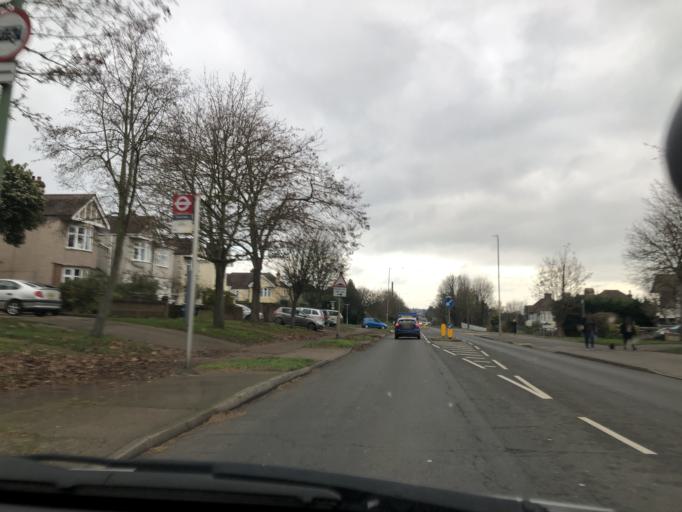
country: GB
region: England
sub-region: Kent
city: Dartford
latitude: 51.4437
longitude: 0.1941
